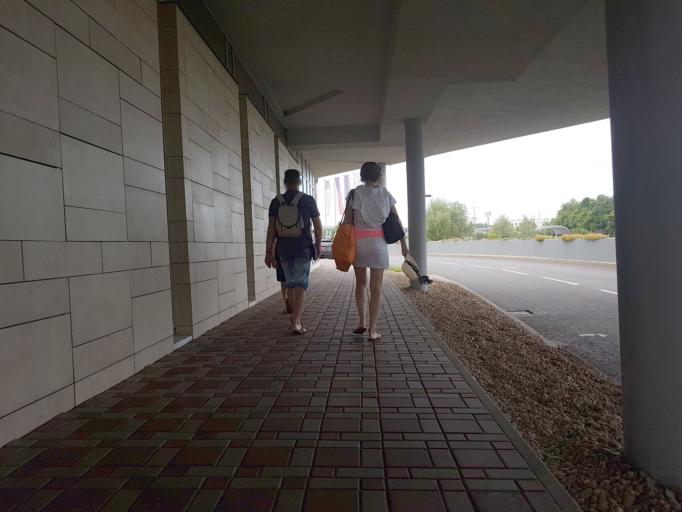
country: CZ
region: Central Bohemia
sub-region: Okres Praha-Zapad
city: Pruhonice
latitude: 50.0079
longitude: 14.5706
